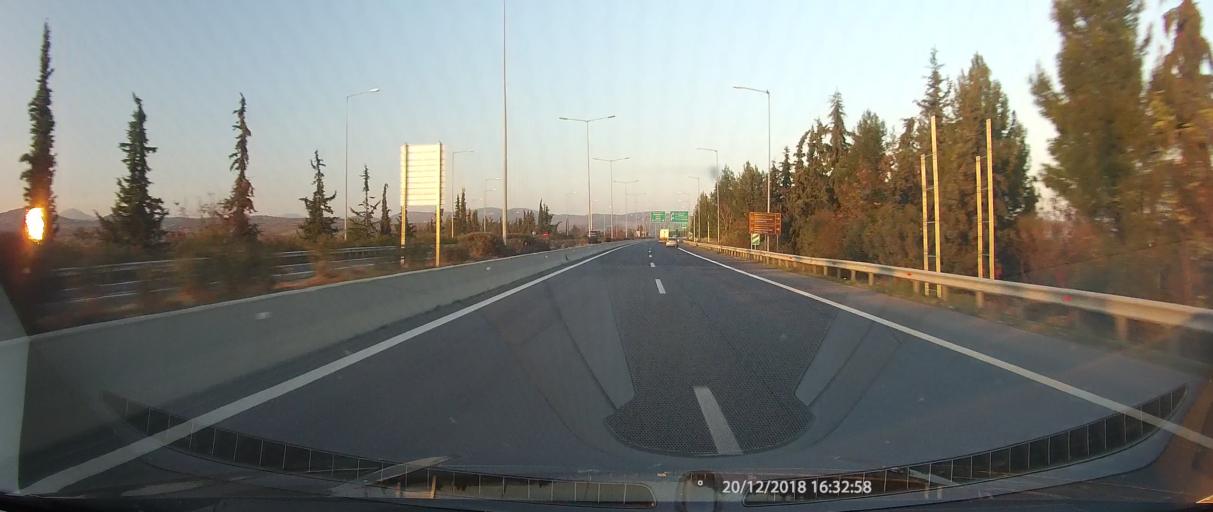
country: GR
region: Thessaly
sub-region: Nomos Magnisias
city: Evxinoupolis
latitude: 39.2550
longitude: 22.7357
